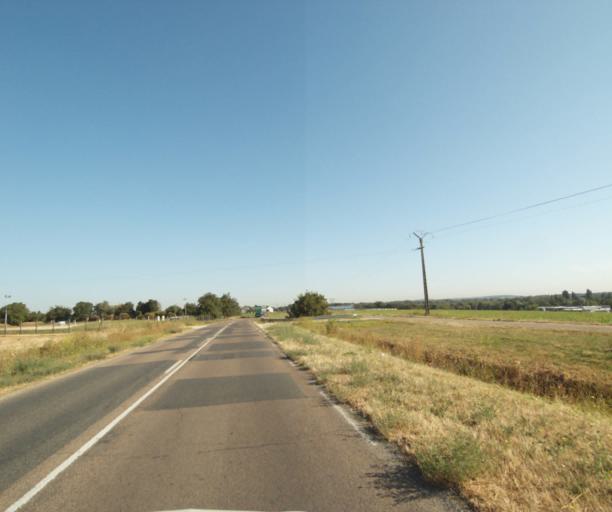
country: FR
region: Ile-de-France
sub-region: Departement de l'Essonne
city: Itteville
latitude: 48.5172
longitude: 2.3552
